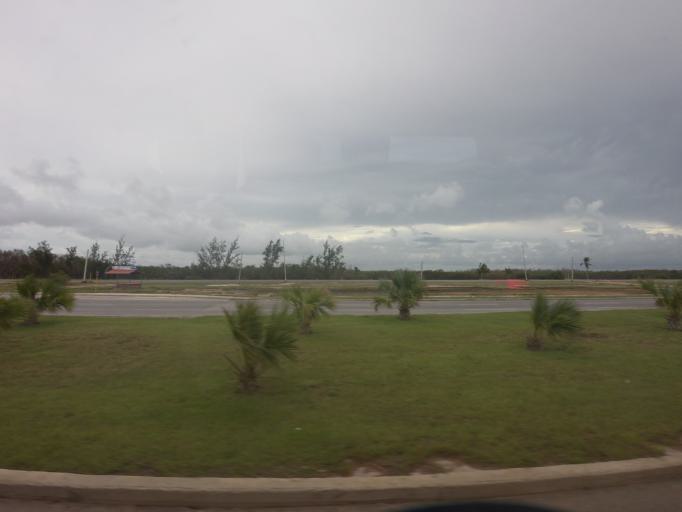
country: CU
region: Matanzas
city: Varadero
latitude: 23.1870
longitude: -81.1711
